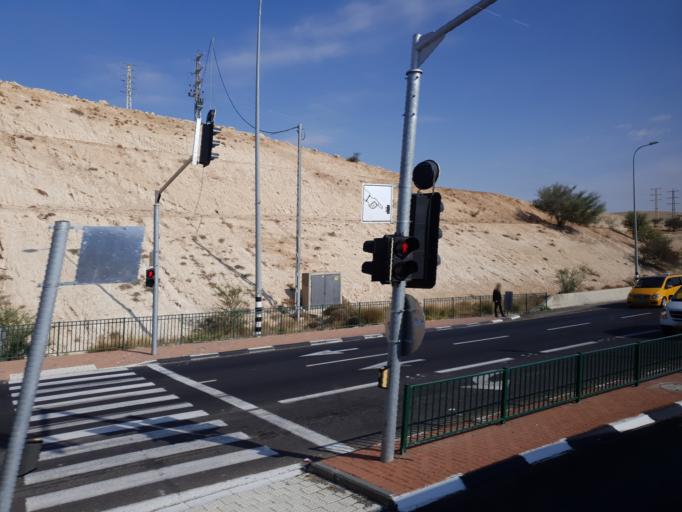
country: PS
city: Az Za`ayyim
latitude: 31.7996
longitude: 35.3119
